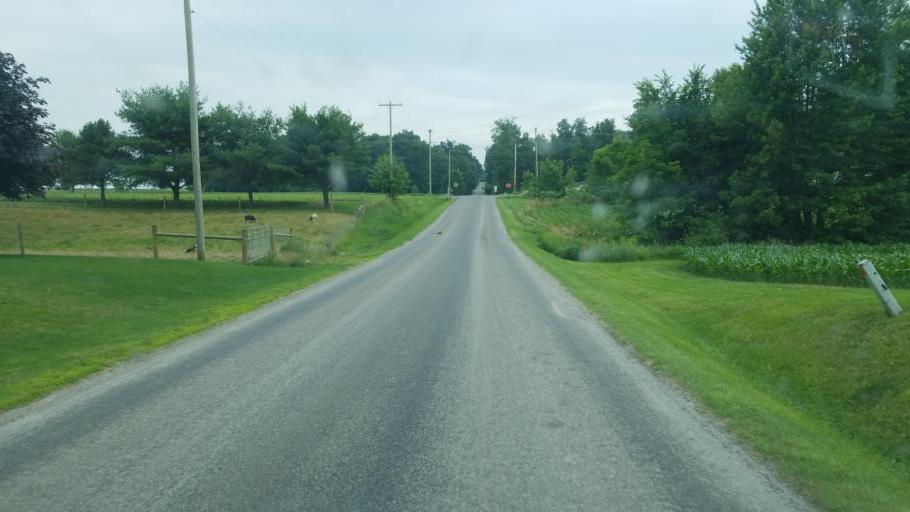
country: US
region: Ohio
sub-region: Wayne County
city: Apple Creek
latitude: 40.7572
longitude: -81.7753
